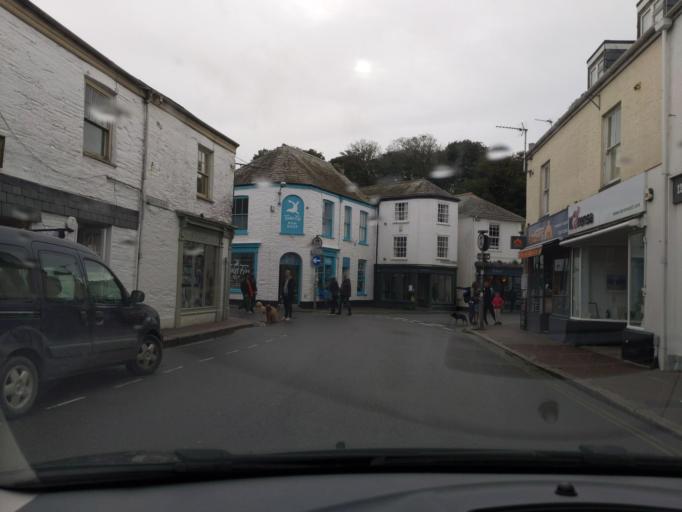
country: GB
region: England
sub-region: Cornwall
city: Padstow
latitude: 50.5411
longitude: -4.9386
